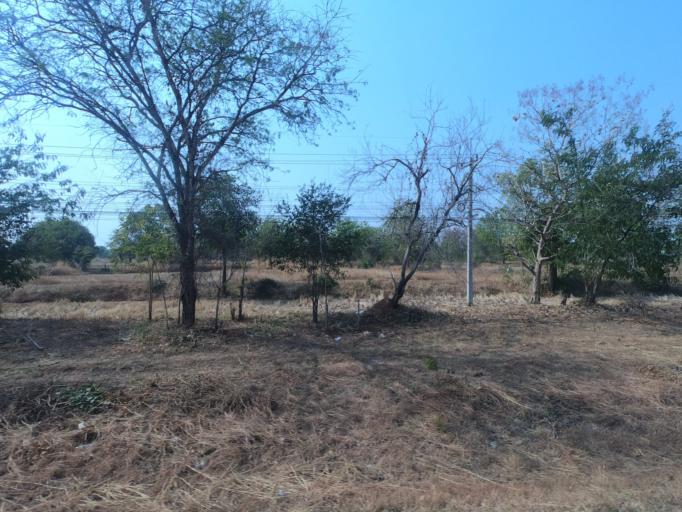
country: TH
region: Nakhon Ratchasima
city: Non Daeng
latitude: 15.3693
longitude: 102.4565
